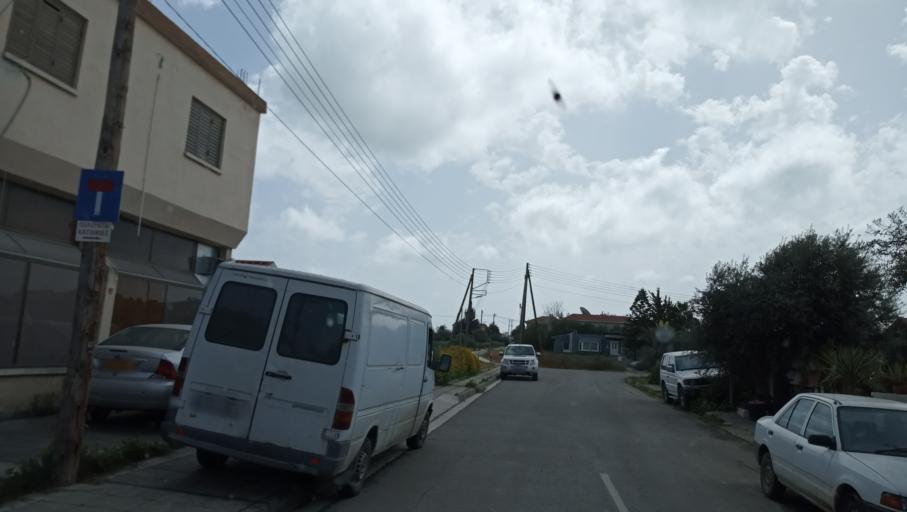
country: CY
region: Lefkosia
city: Dali
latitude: 35.0281
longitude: 33.4250
